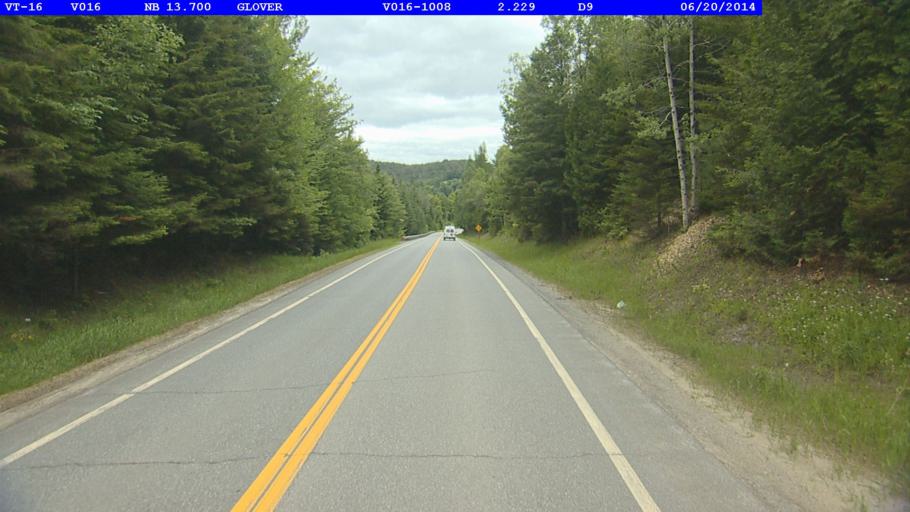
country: US
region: Vermont
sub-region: Caledonia County
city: Hardwick
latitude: 44.6562
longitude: -72.1973
